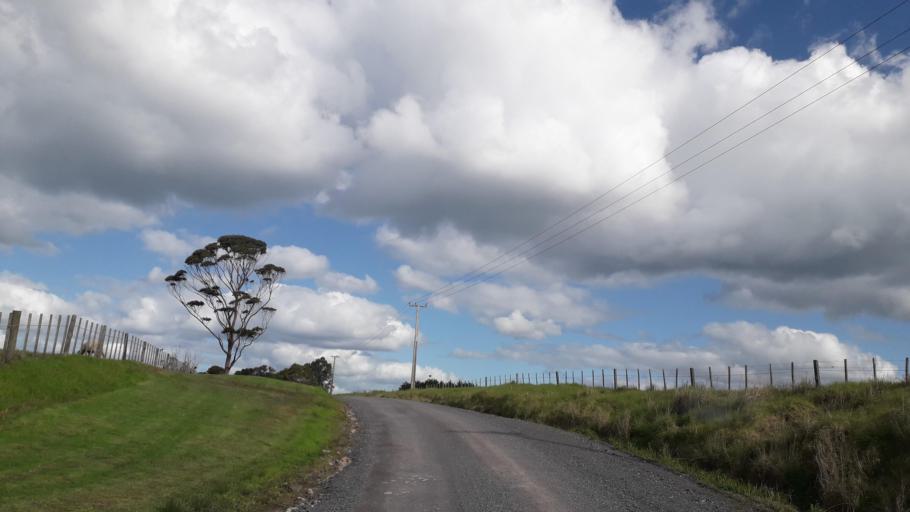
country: NZ
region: Northland
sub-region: Far North District
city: Kerikeri
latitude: -35.1501
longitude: 174.0396
